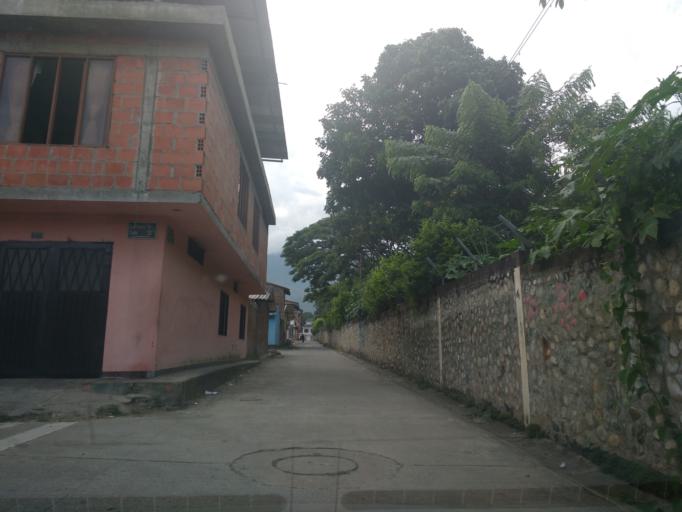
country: CO
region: Cauca
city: Miranda
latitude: 3.2581
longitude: -76.2300
